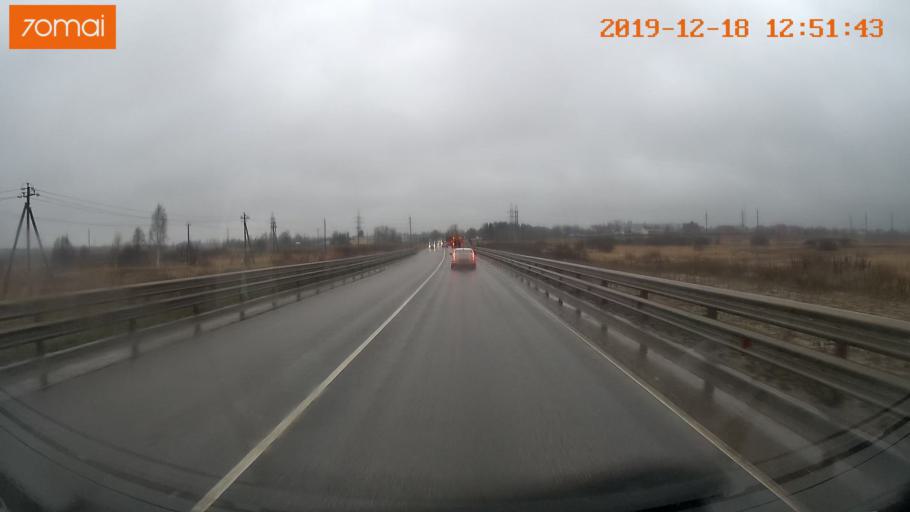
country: RU
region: Moskovskaya
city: Klin
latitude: 56.3058
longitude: 36.6849
